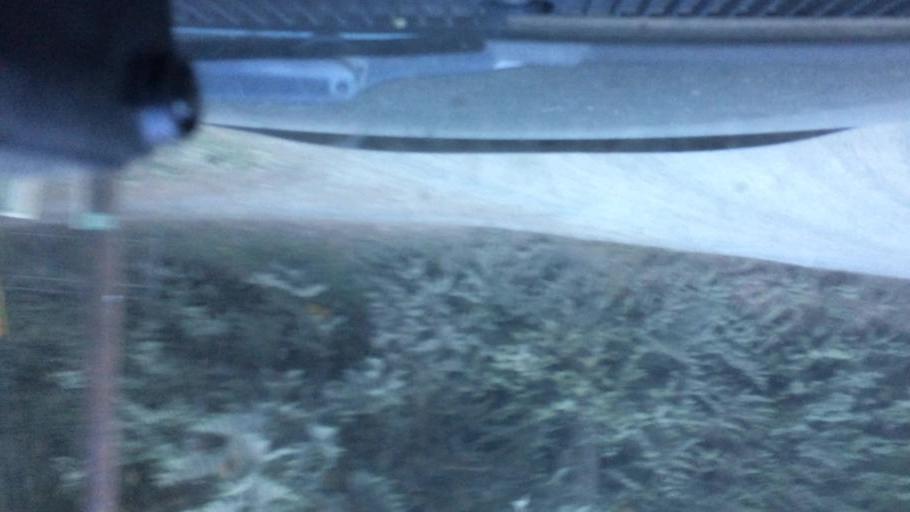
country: US
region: Oregon
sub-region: Yamhill County
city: Newberg
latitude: 45.3608
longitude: -122.9802
